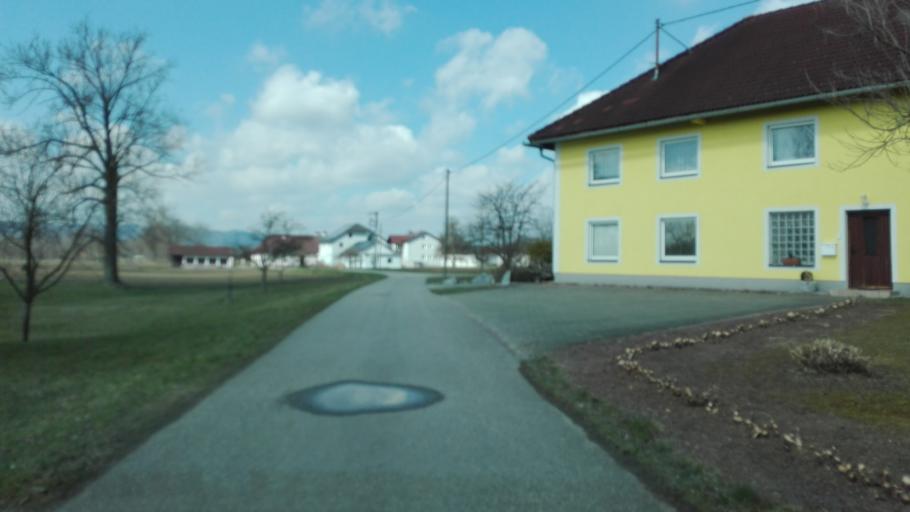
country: AT
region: Upper Austria
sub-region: Politischer Bezirk Urfahr-Umgebung
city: Feldkirchen an der Donau
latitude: 48.3395
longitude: 14.0497
